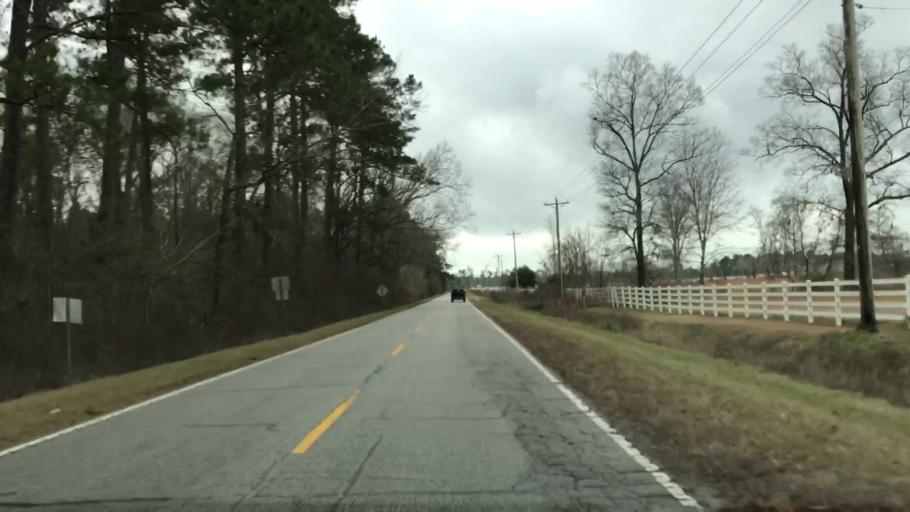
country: US
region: South Carolina
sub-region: Florence County
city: Johnsonville
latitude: 33.6577
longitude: -79.4191
